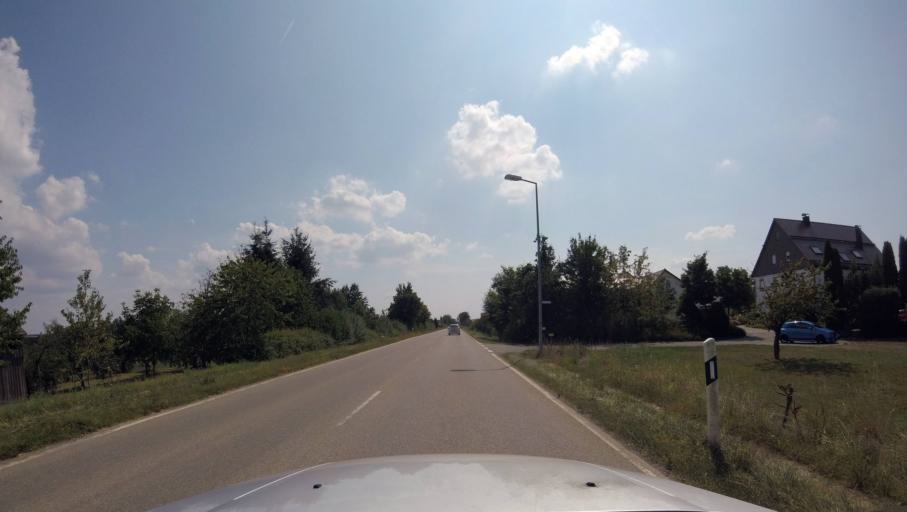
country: DE
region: Baden-Wuerttemberg
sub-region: Regierungsbezirk Stuttgart
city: Welzheim
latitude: 48.9037
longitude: 9.6253
